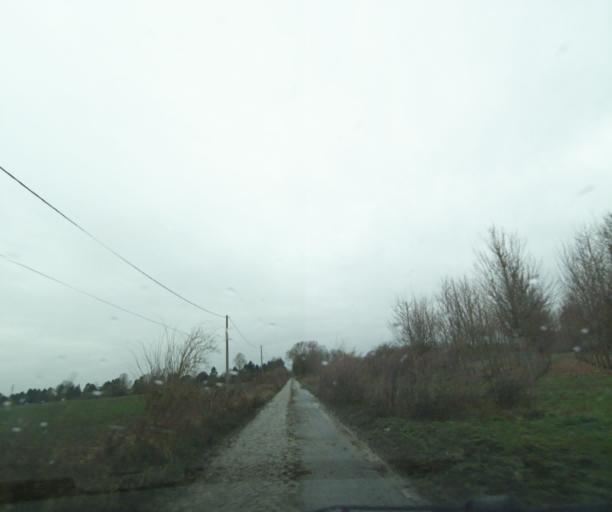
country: FR
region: Nord-Pas-de-Calais
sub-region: Departement du Nord
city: Vicq
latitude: 50.4258
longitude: 3.6018
